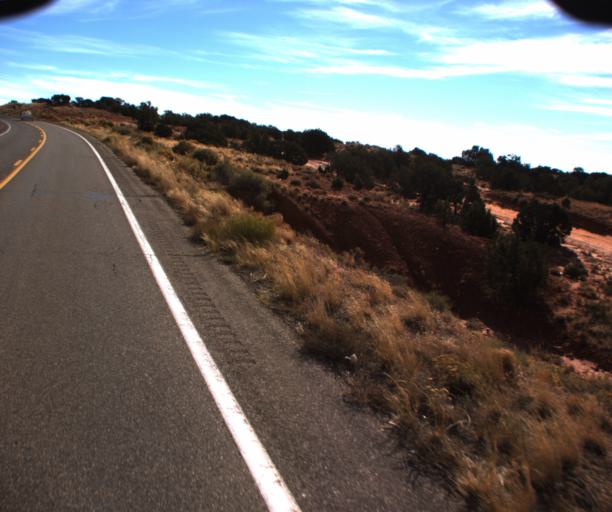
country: US
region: Arizona
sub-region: Coconino County
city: Kaibito
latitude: 36.5761
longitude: -111.1230
